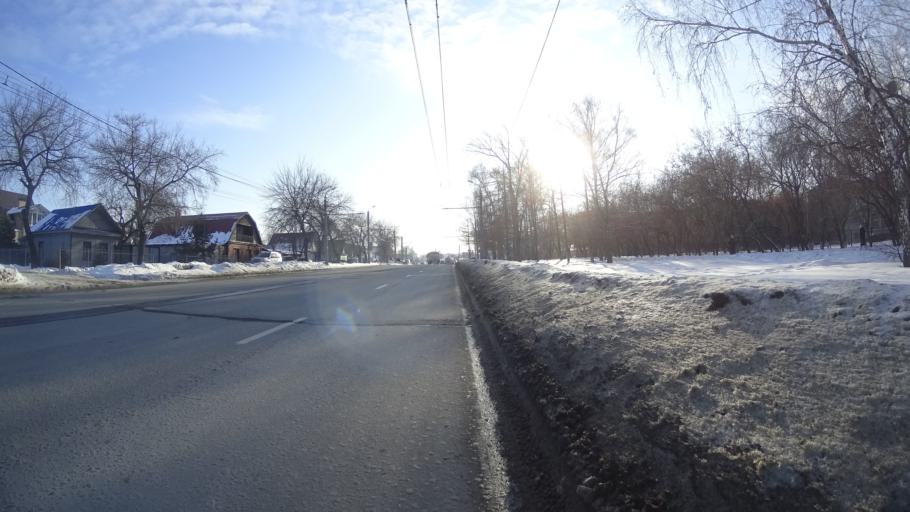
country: RU
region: Chelyabinsk
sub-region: Gorod Chelyabinsk
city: Chelyabinsk
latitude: 55.1854
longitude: 61.4596
